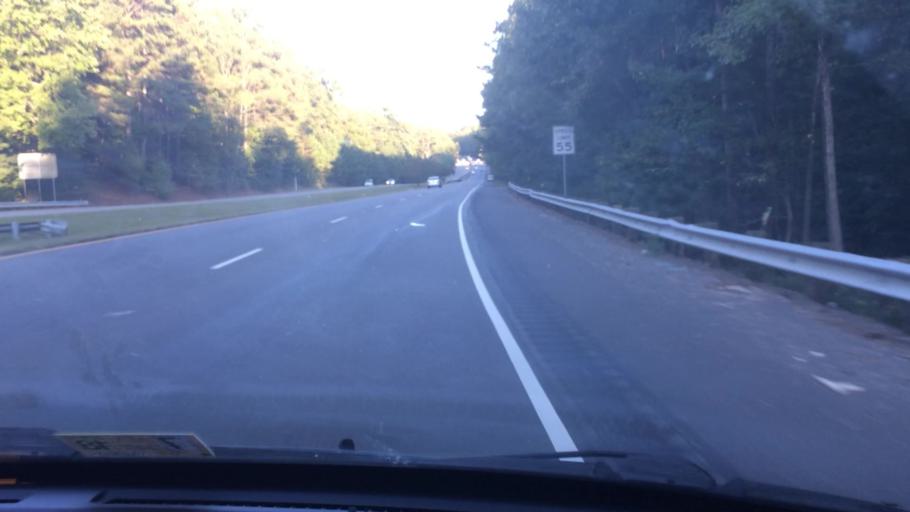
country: US
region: Virginia
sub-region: City of Williamsburg
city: Williamsburg
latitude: 37.2488
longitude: -76.6975
